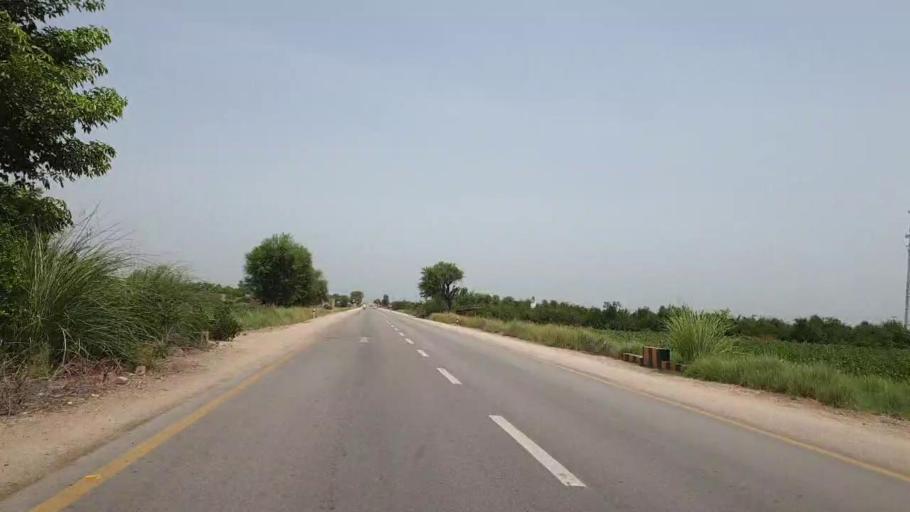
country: PK
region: Sindh
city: Shahpur Chakar
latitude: 26.1582
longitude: 68.6322
